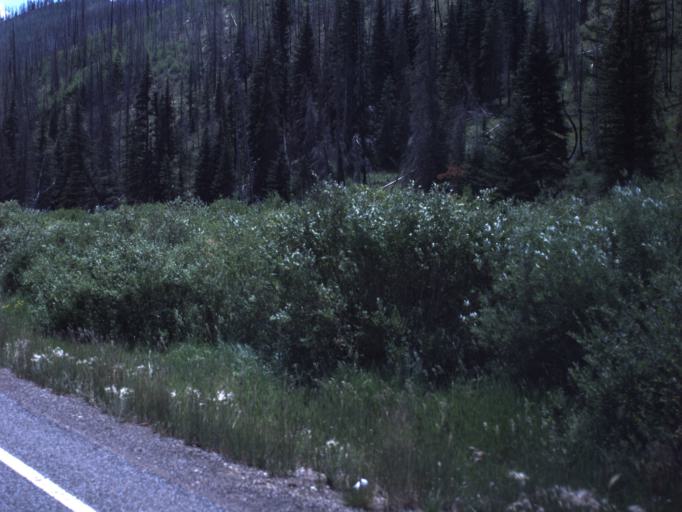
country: US
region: Utah
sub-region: Sanpete County
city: Fairview
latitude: 39.5660
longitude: -111.1780
